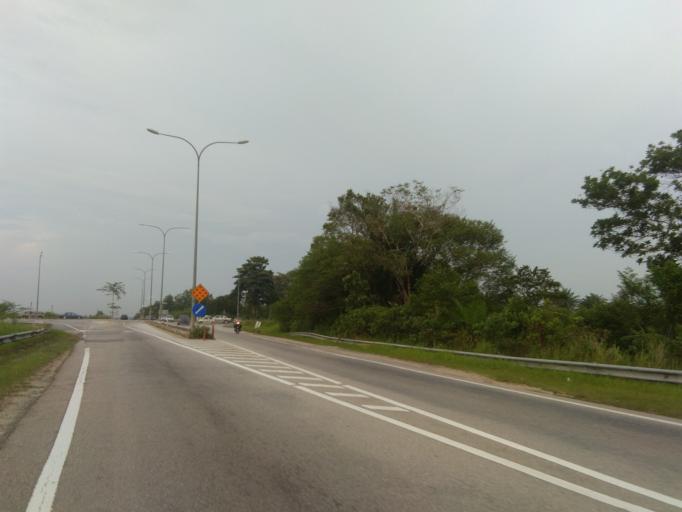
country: MY
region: Penang
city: Tasek Glugor
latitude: 5.5120
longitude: 100.6294
